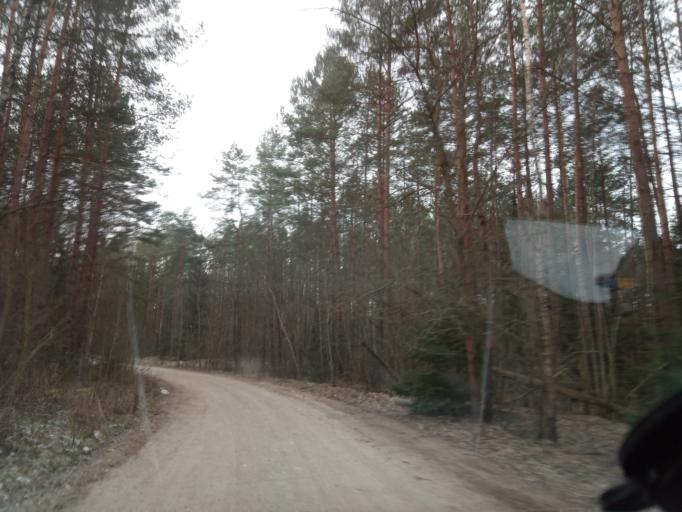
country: LT
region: Alytaus apskritis
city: Varena
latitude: 53.9960
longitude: 24.3483
